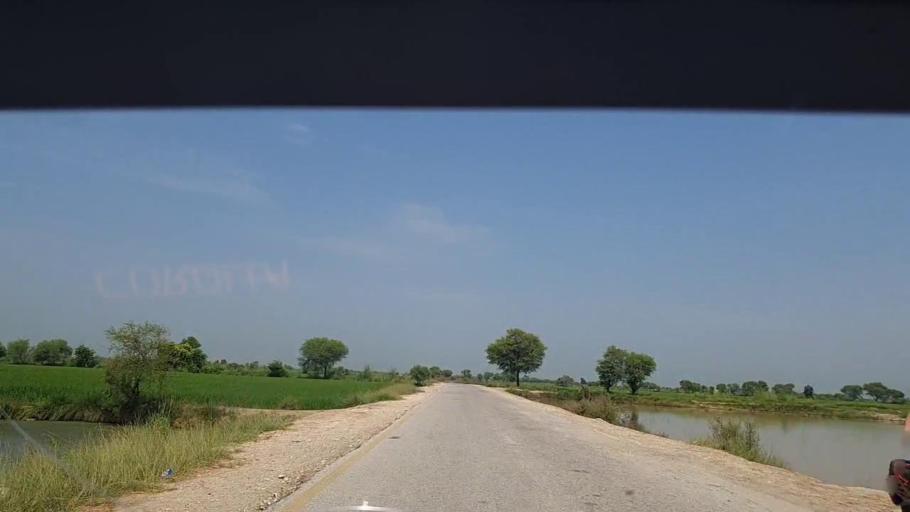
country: PK
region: Sindh
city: Thul
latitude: 28.1306
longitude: 68.8178
